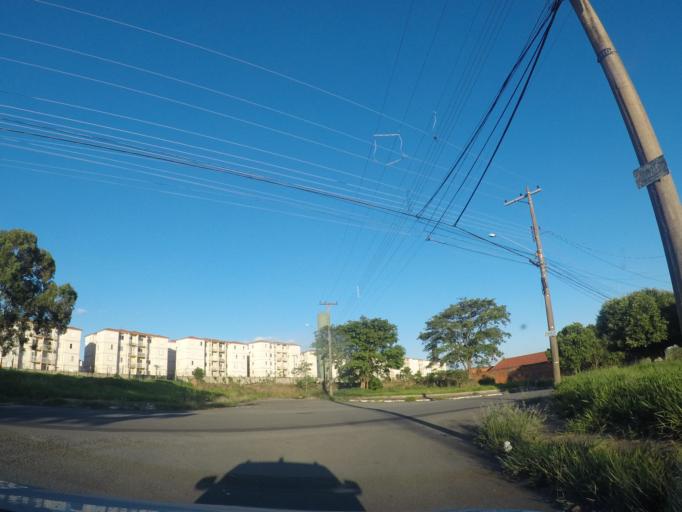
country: BR
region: Sao Paulo
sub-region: Sumare
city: Sumare
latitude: -22.8209
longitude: -47.2509
